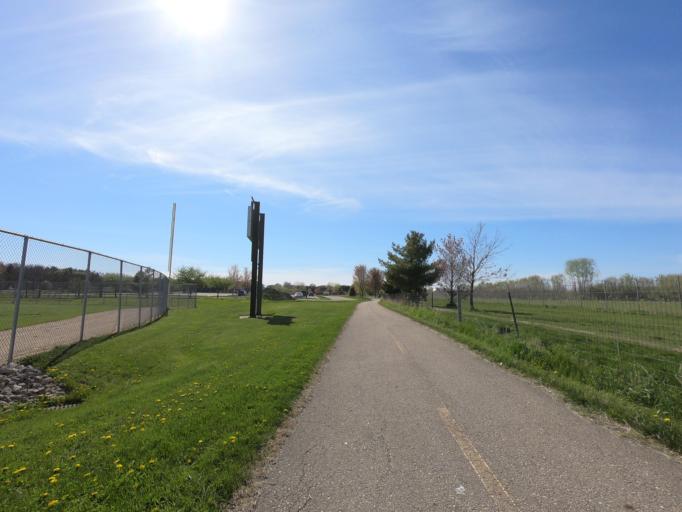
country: US
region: Wisconsin
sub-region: Dane County
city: Middleton
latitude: 43.1129
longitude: -89.5394
